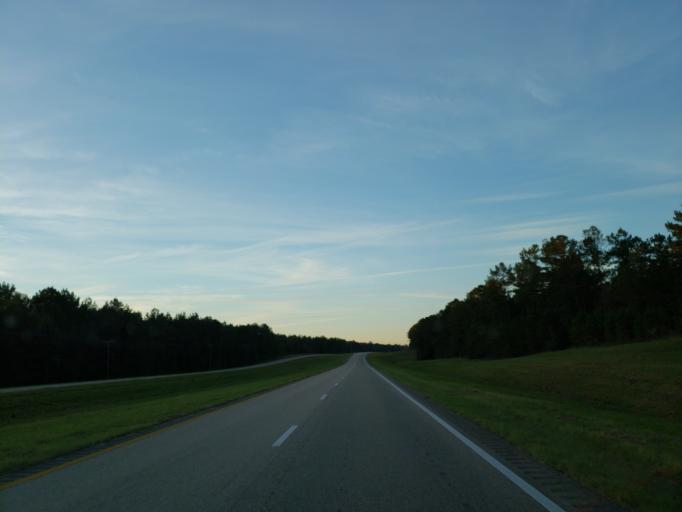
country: US
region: Mississippi
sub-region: Wayne County
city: Belmont
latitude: 31.4869
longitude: -88.4889
